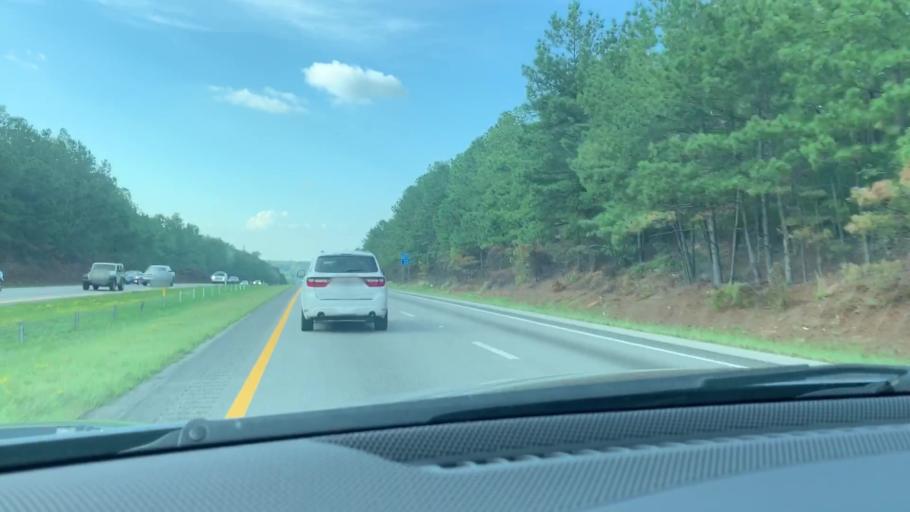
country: US
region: South Carolina
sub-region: Calhoun County
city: Oak Grove
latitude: 33.7399
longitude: -80.9374
